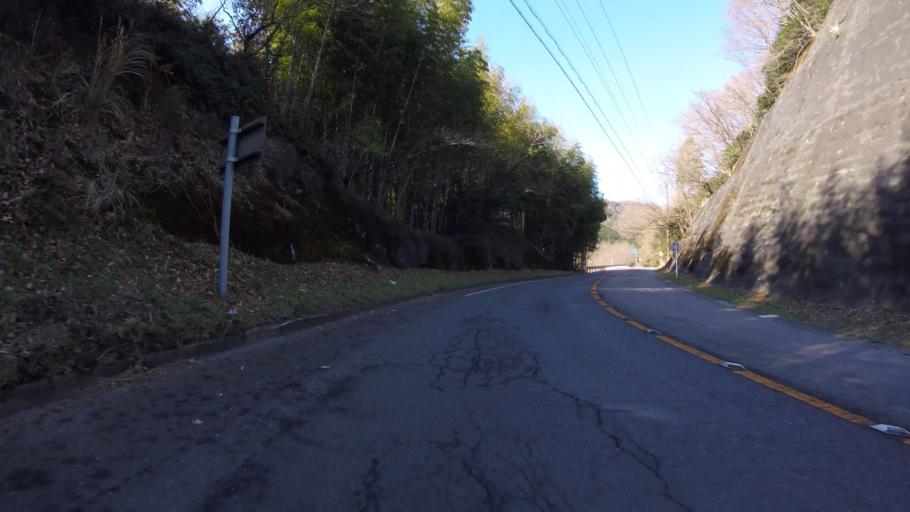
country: JP
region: Shizuoka
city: Ito
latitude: 34.9367
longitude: 139.0642
